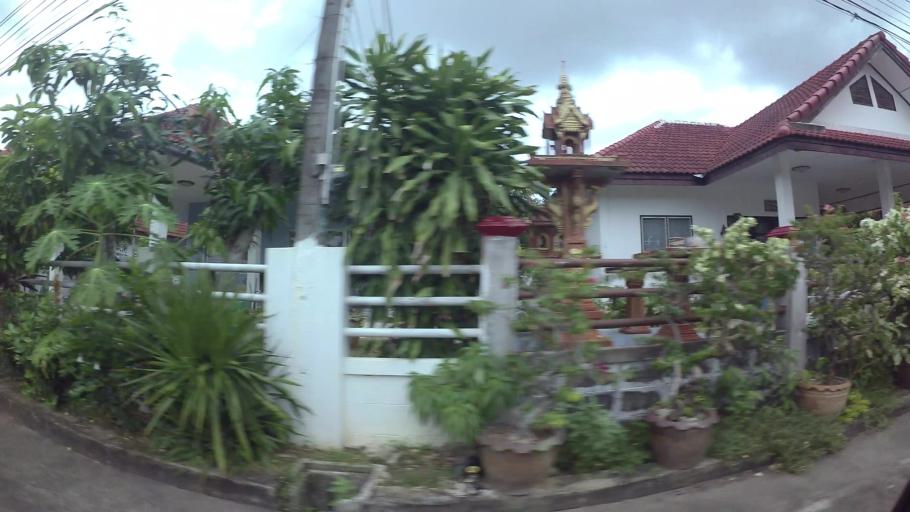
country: TH
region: Chon Buri
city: Sattahip
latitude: 12.7264
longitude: 100.9046
